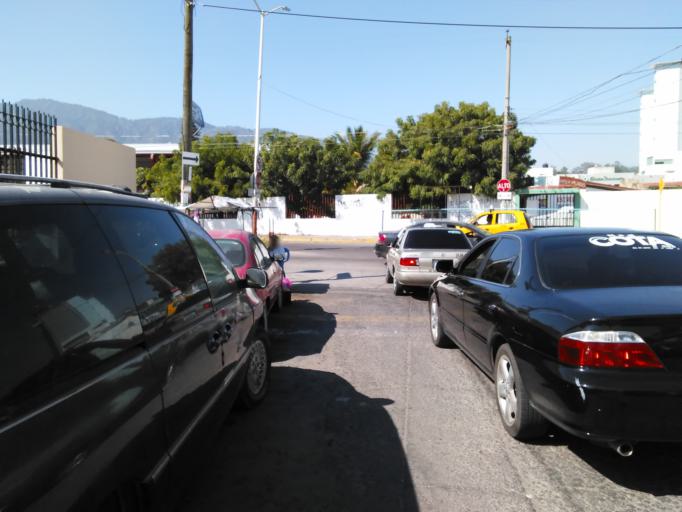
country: MX
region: Nayarit
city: Tepic
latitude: 21.4976
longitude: -104.8922
